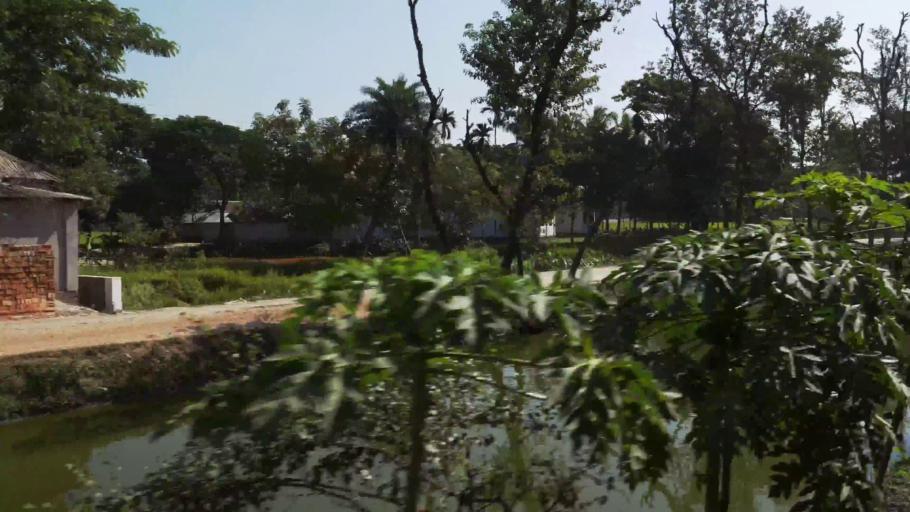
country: BD
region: Dhaka
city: Gafargaon
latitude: 24.5449
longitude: 90.5085
